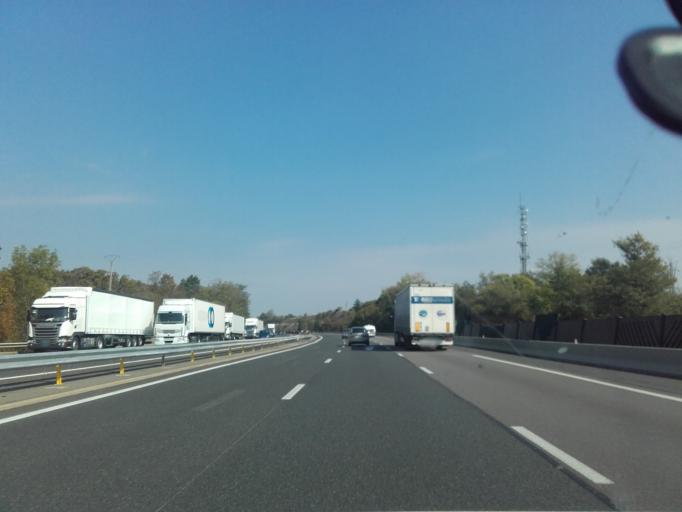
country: FR
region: Bourgogne
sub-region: Departement de Saone-et-Loire
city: Sance
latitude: 46.3276
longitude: 4.8123
